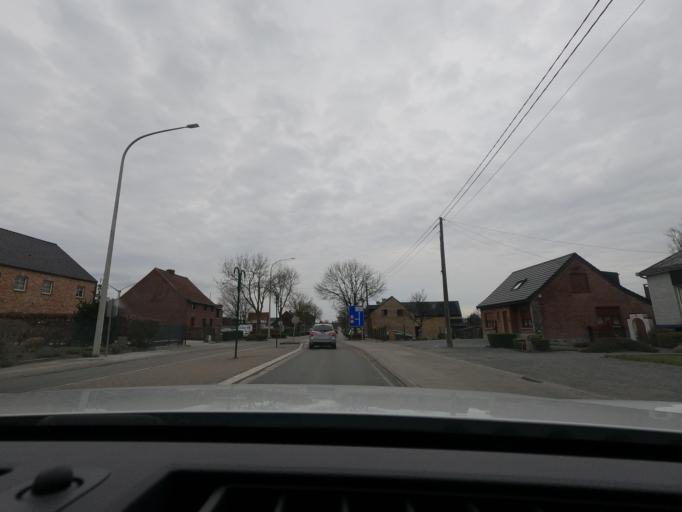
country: BE
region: Wallonia
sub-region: Province du Hainaut
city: Silly
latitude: 50.6537
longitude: 3.8735
